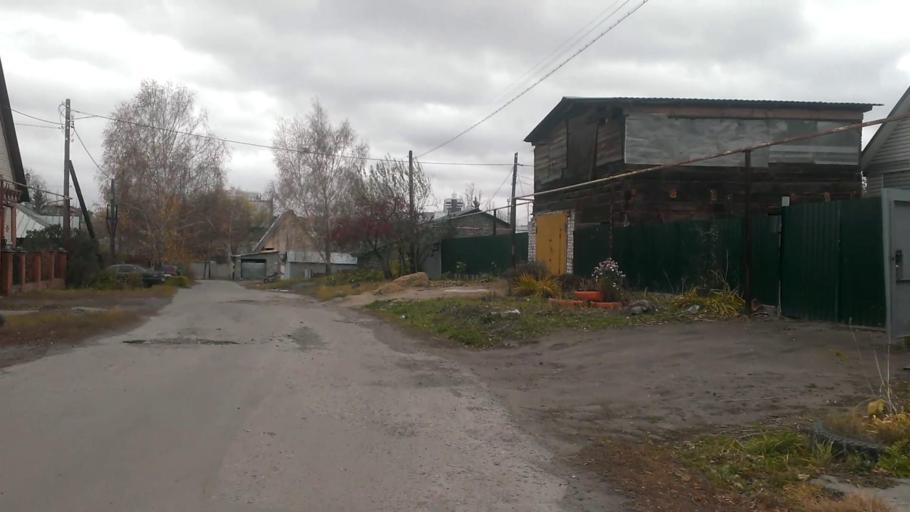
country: RU
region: Altai Krai
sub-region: Gorod Barnaulskiy
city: Barnaul
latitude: 53.3513
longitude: 83.7478
